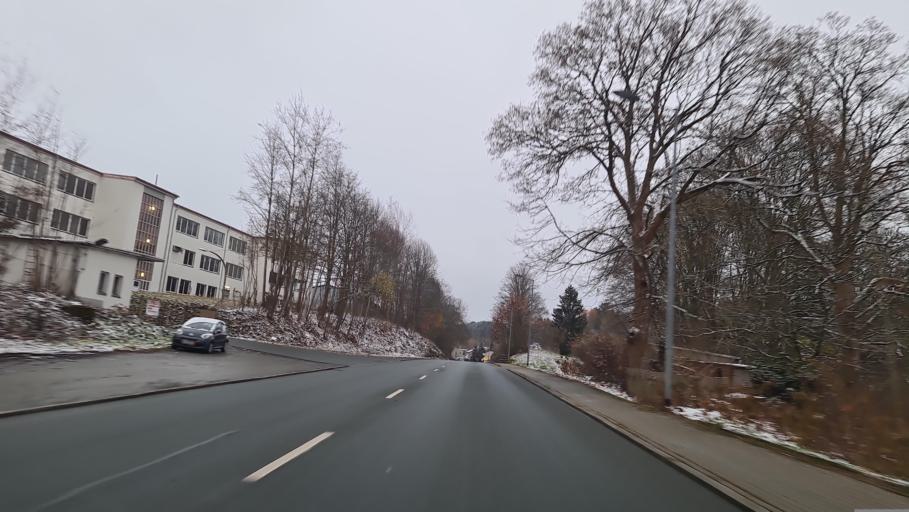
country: DE
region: Saxony
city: Markneukirchen
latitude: 50.3139
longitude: 12.3372
